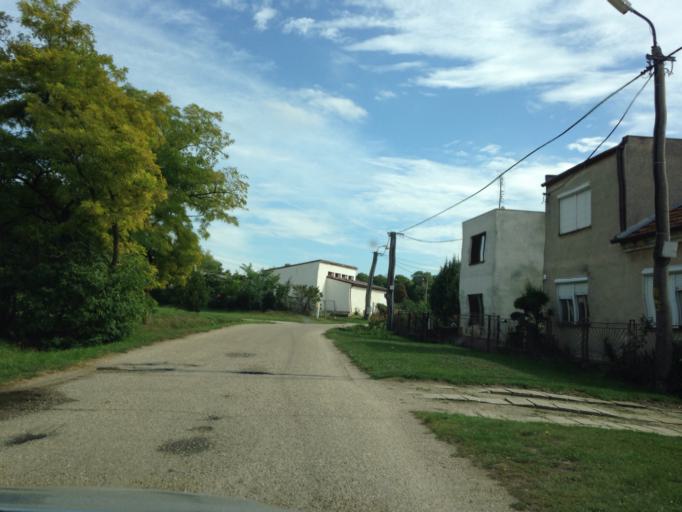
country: SK
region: Nitriansky
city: Svodin
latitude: 47.9060
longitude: 18.4195
